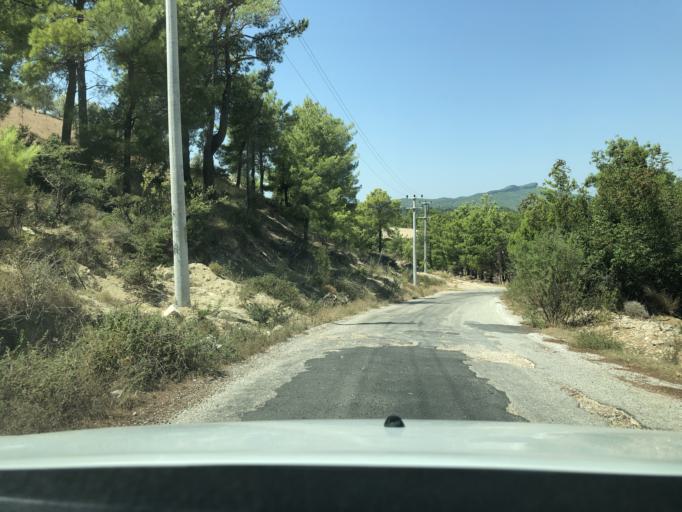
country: TR
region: Antalya
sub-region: Manavgat
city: Kizilagac
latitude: 36.8646
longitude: 31.5599
